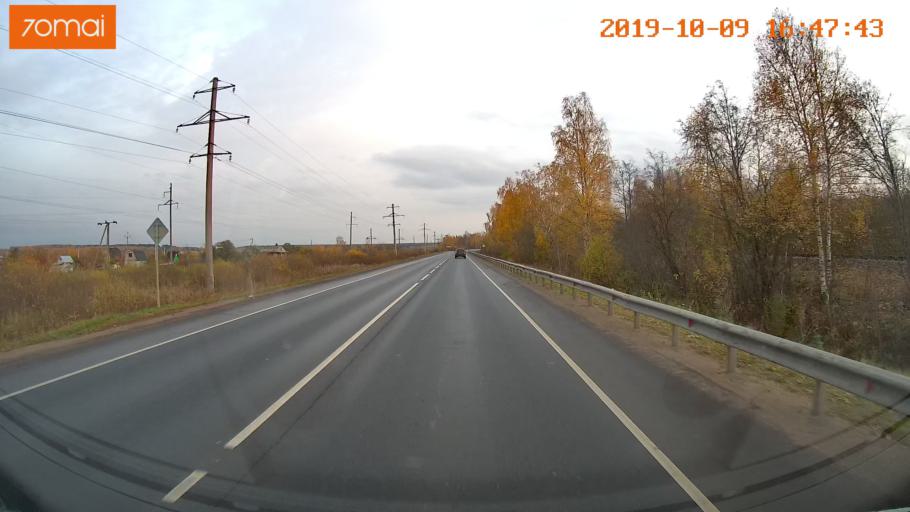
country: RU
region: Kostroma
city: Volgorechensk
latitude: 57.4345
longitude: 41.1828
